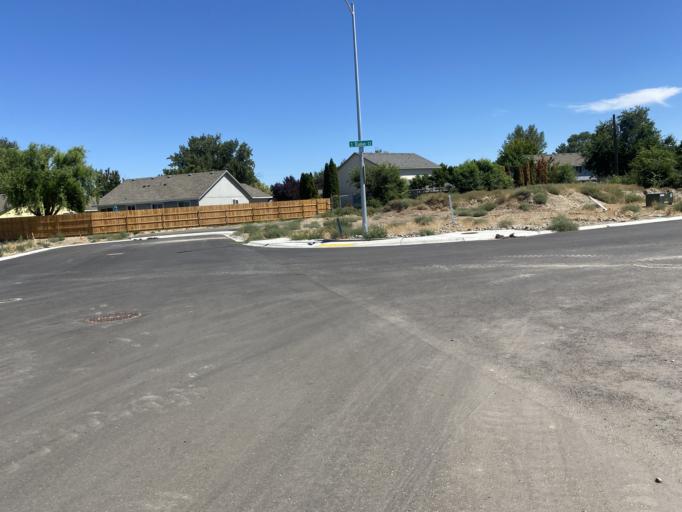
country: US
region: Washington
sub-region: Benton County
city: Kennewick
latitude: 46.2042
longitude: -119.1738
